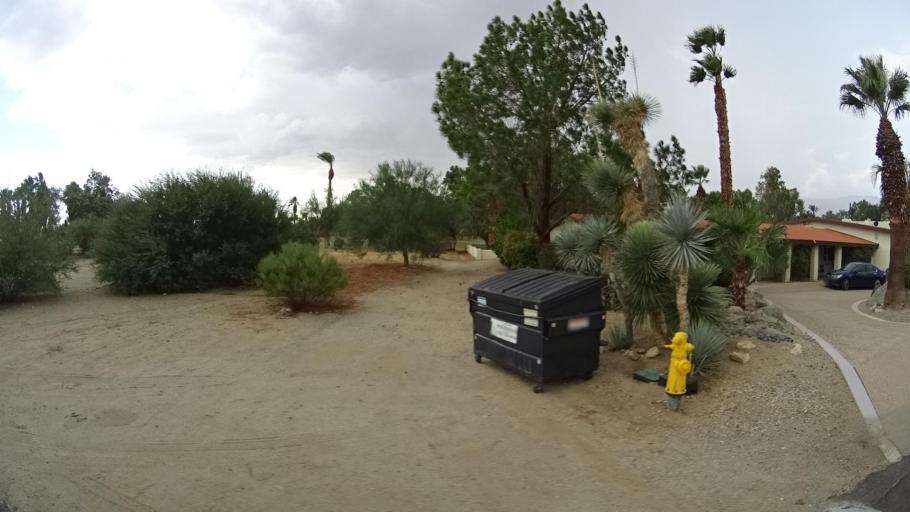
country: US
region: California
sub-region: San Diego County
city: Borrego Springs
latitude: 33.2873
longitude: -116.3904
